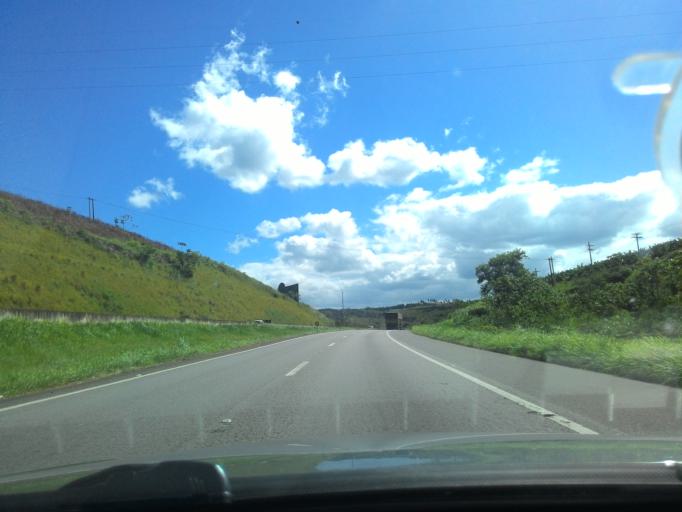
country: BR
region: Sao Paulo
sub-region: Cajati
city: Cajati
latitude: -24.7394
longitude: -48.1237
